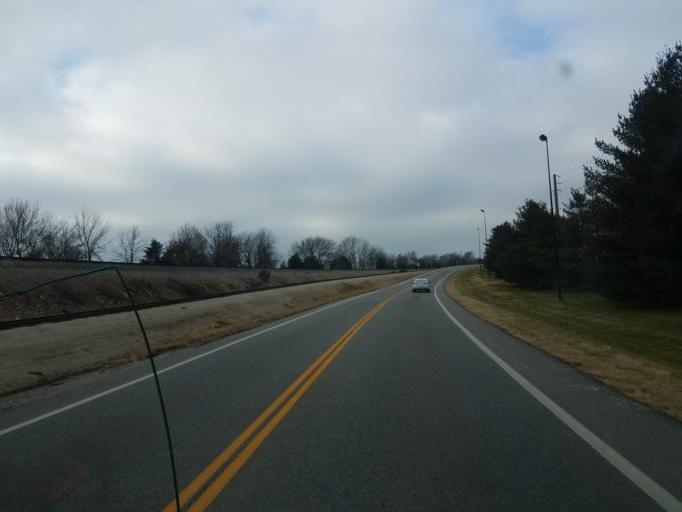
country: US
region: Missouri
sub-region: Greene County
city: Strafford
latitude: 37.2392
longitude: -93.1999
